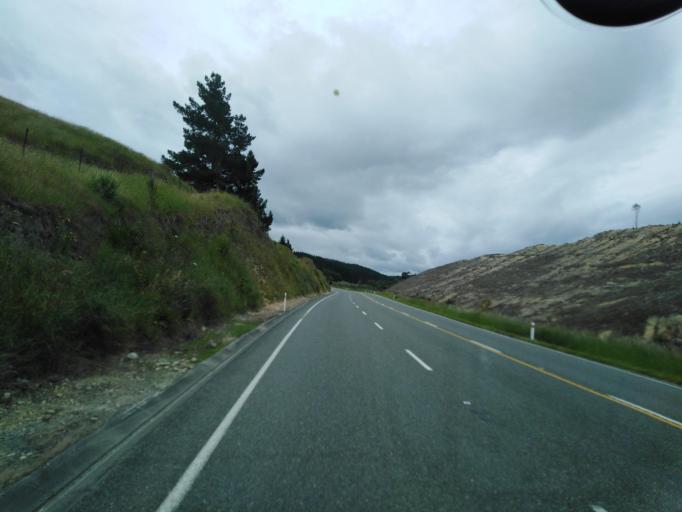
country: NZ
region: Tasman
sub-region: Tasman District
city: Wakefield
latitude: -41.4659
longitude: 172.9463
